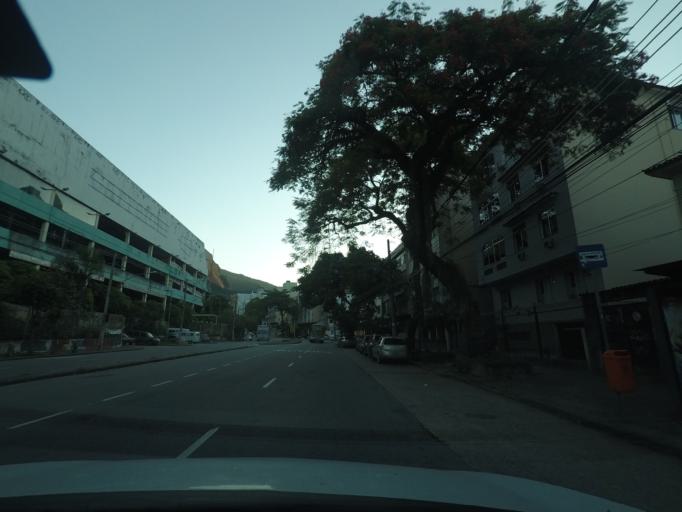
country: BR
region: Rio de Janeiro
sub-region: Rio De Janeiro
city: Rio de Janeiro
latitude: -22.9420
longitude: -43.2529
